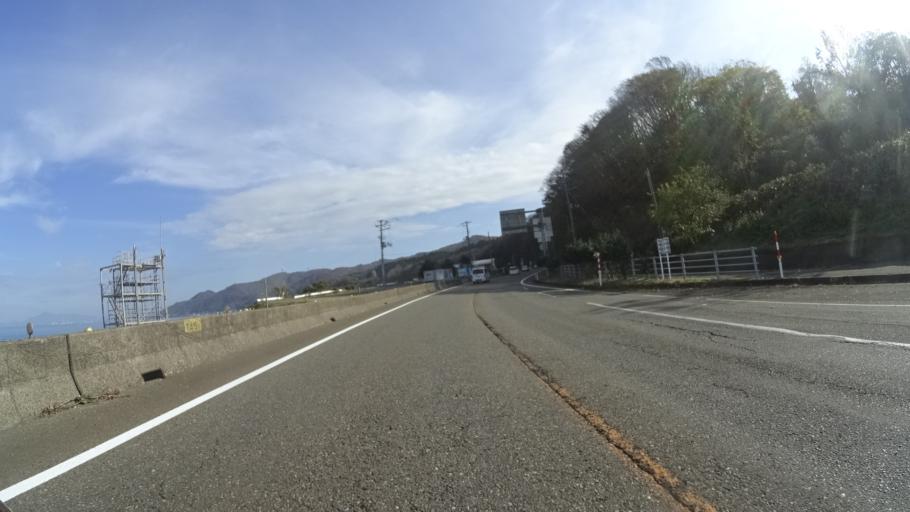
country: JP
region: Niigata
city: Joetsu
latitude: 37.1631
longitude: 138.1468
